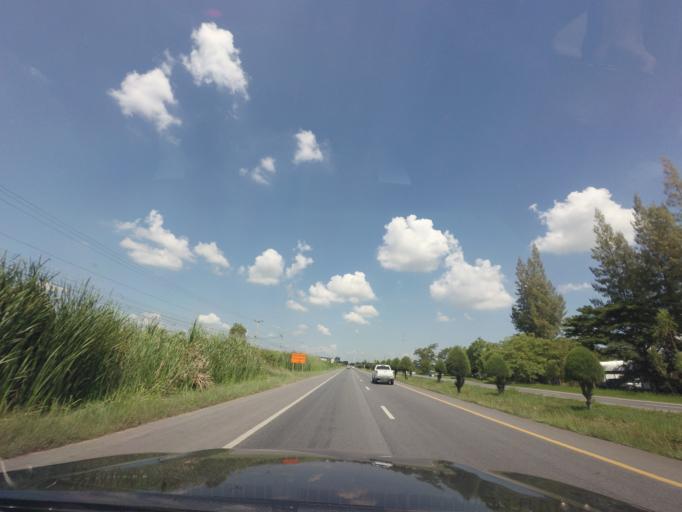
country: TH
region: Nakhon Ratchasima
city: Nakhon Ratchasima
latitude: 15.0548
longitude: 102.1454
